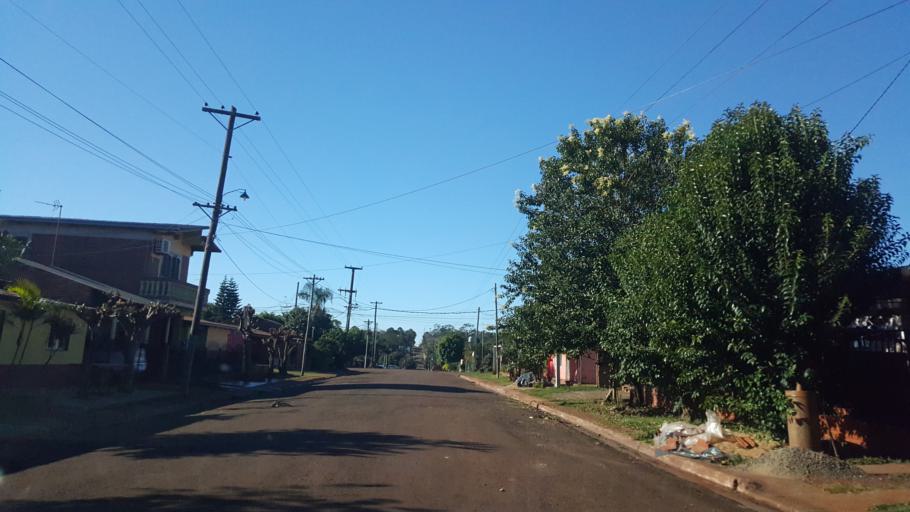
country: AR
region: Misiones
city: Gobernador Roca
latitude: -27.1964
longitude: -55.4741
